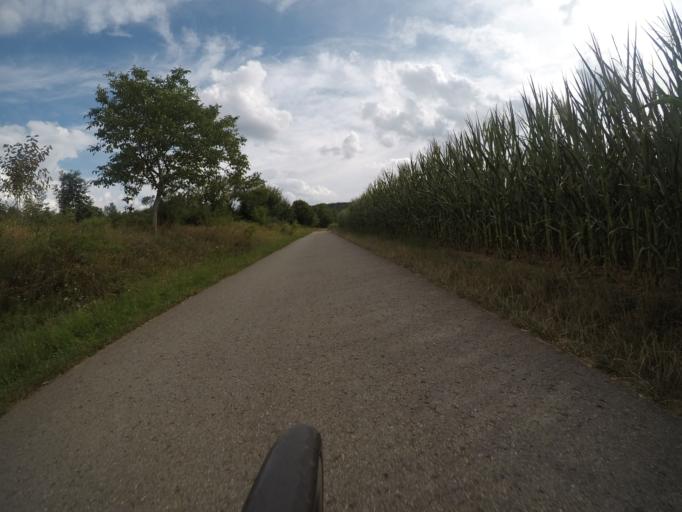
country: DE
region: Baden-Wuerttemberg
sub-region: Regierungsbezirk Stuttgart
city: Weil der Stadt
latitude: 48.7328
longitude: 8.8838
